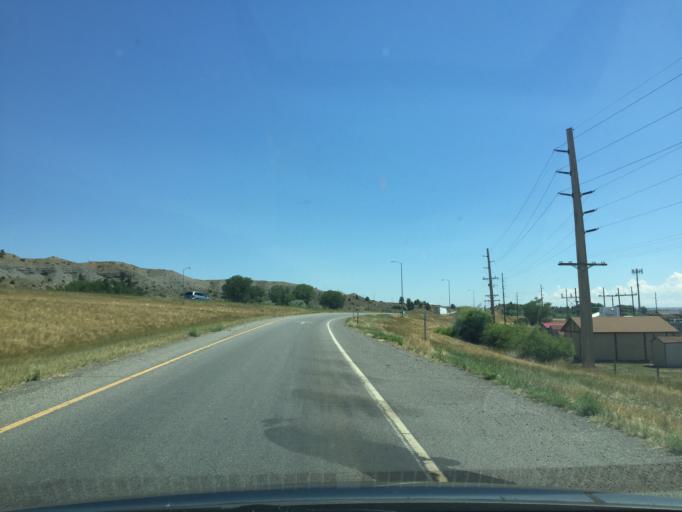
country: US
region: Montana
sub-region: Stillwater County
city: Columbus
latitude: 45.6456
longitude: -109.2470
